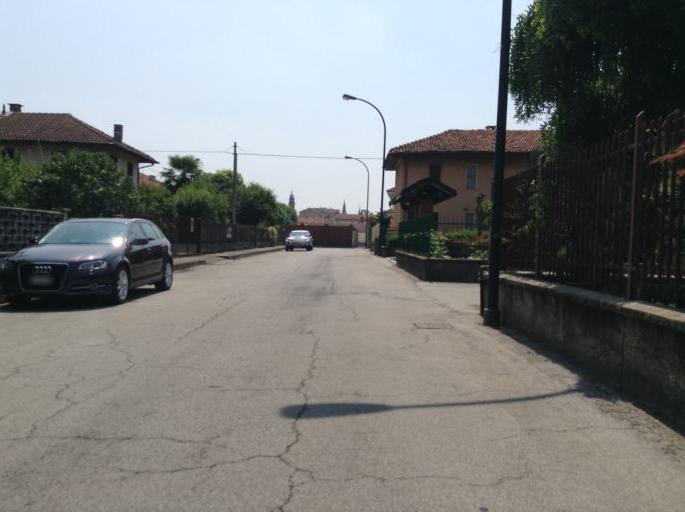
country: IT
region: Piedmont
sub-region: Provincia di Torino
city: Carignano
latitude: 44.9128
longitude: 7.6752
